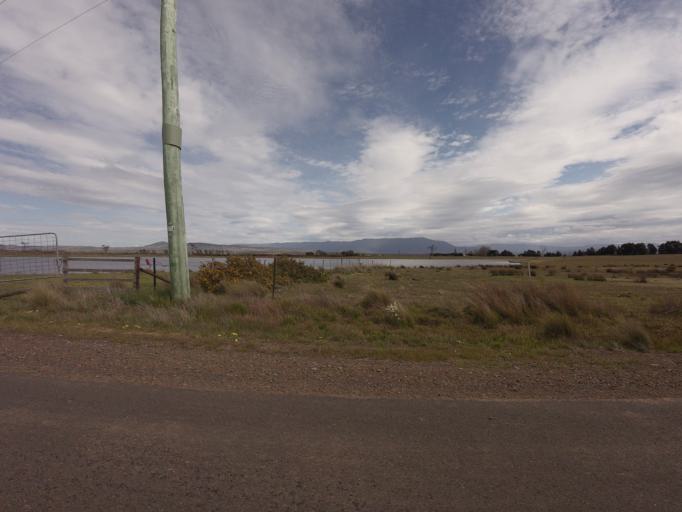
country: AU
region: Tasmania
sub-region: Northern Midlands
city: Evandale
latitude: -41.8275
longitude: 147.3223
